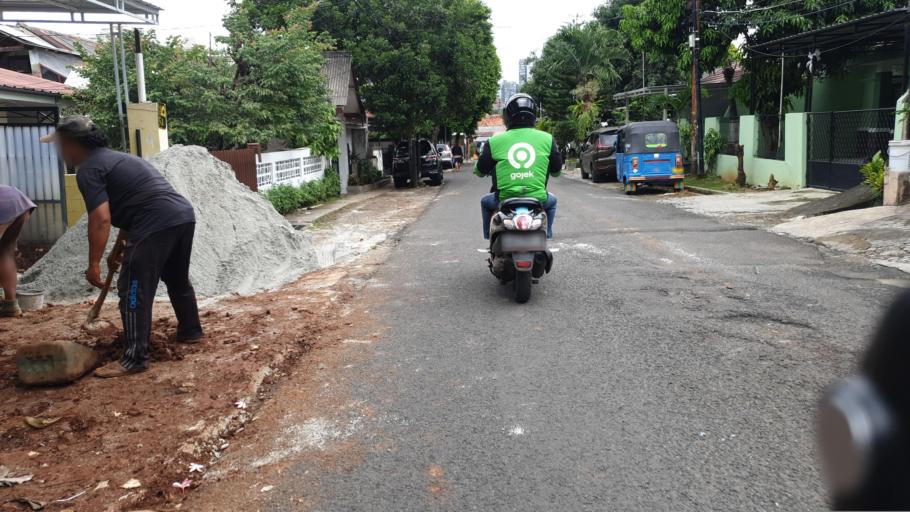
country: ID
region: Jakarta Raya
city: Jakarta
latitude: -6.2541
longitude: 106.7841
